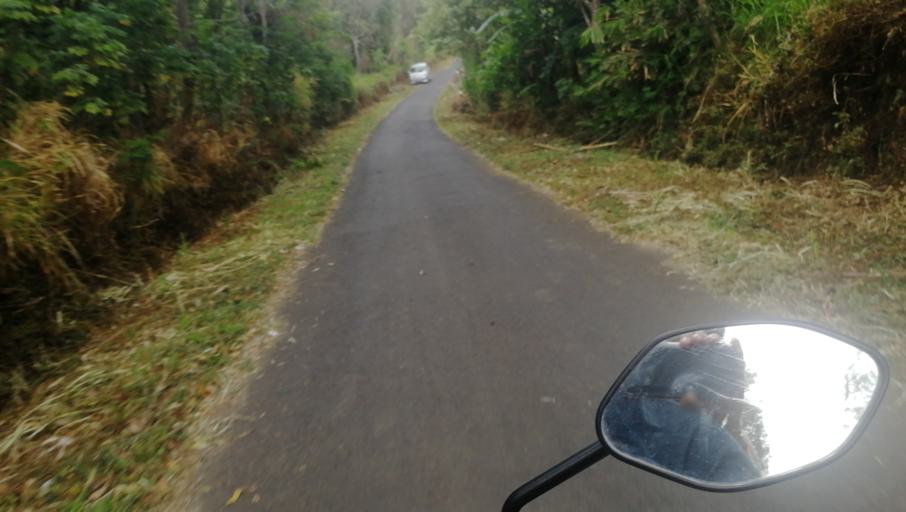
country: ID
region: Bali
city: Munduk
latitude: -8.2236
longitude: 115.1106
